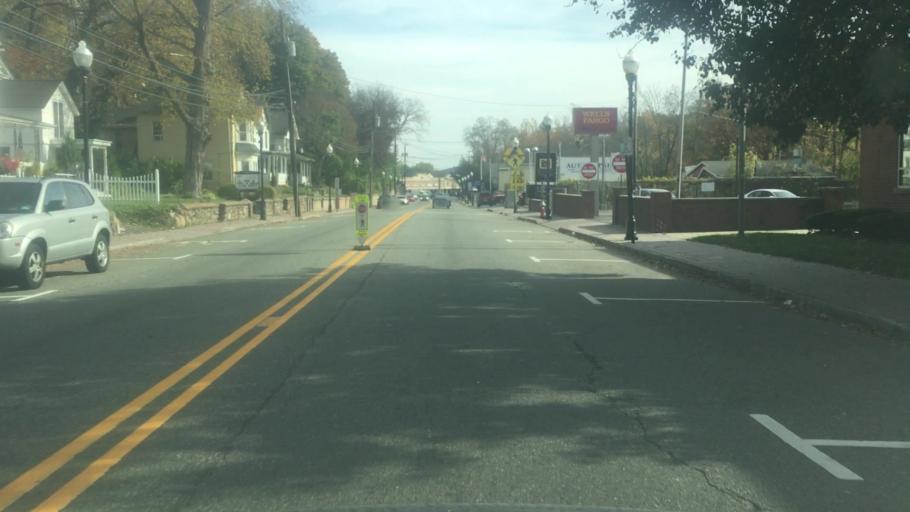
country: US
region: New Jersey
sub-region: Passaic County
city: Bloomingdale
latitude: 41.0036
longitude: -74.3330
